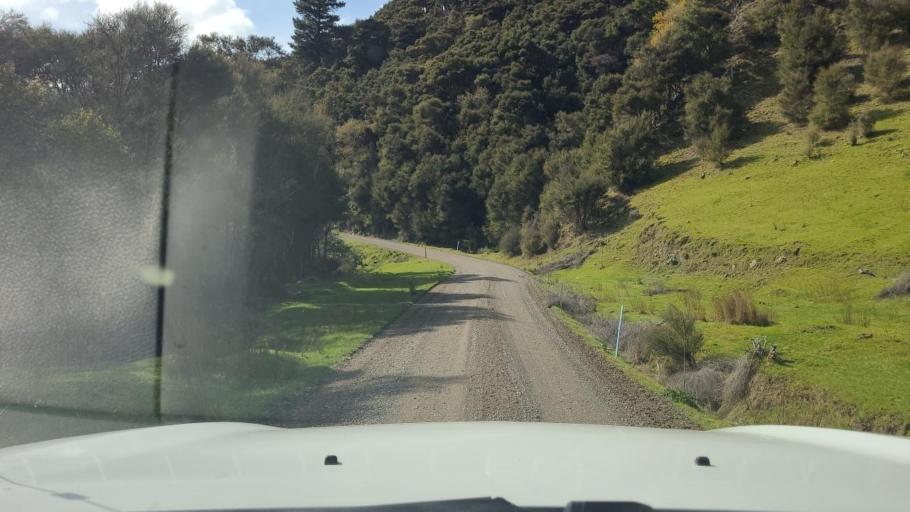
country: NZ
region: Wellington
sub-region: South Wairarapa District
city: Waipawa
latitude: -41.3519
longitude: 175.6854
